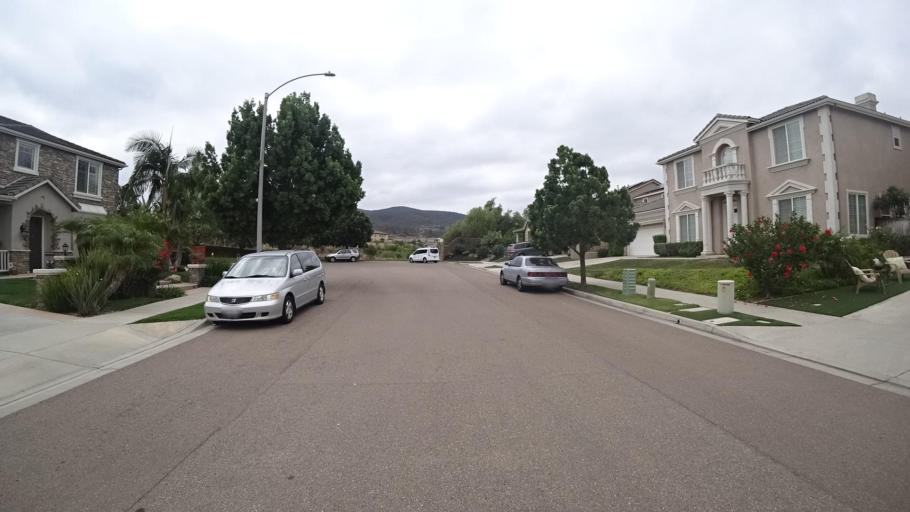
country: US
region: California
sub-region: San Diego County
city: Fairbanks Ranch
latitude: 32.9992
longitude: -117.1079
